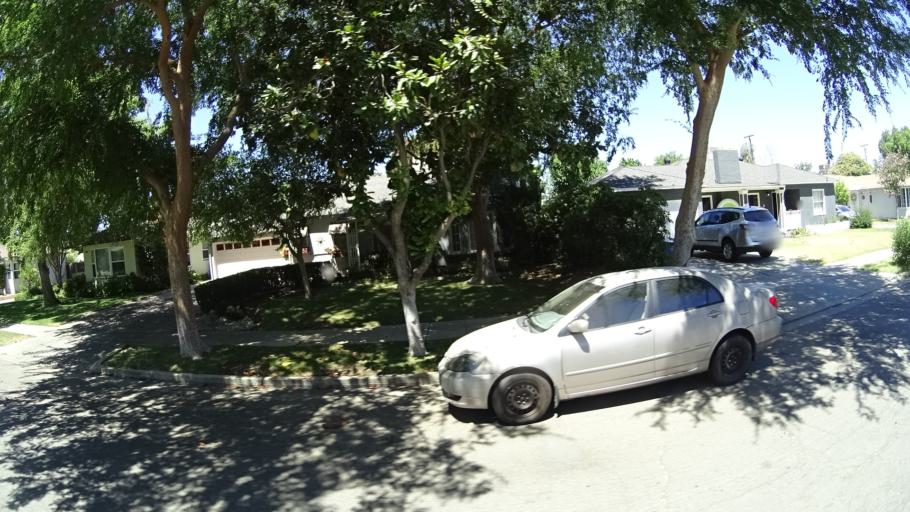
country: US
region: California
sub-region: Fresno County
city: Fresno
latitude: 36.7728
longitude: -119.8142
